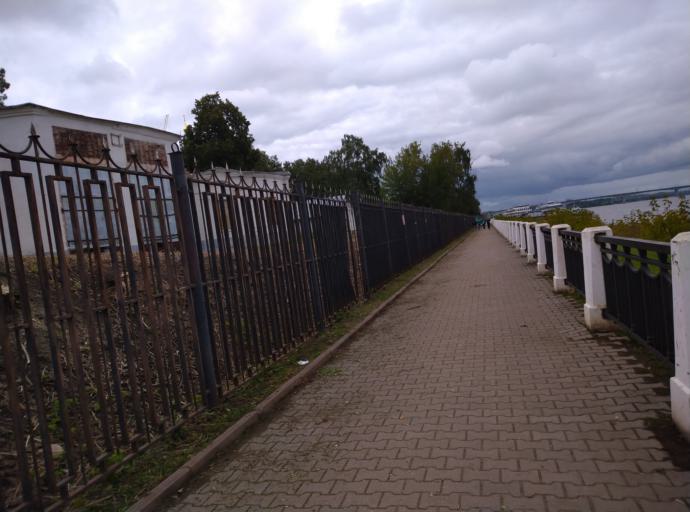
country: RU
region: Kostroma
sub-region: Kostromskoy Rayon
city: Kostroma
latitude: 57.7640
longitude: 40.9220
